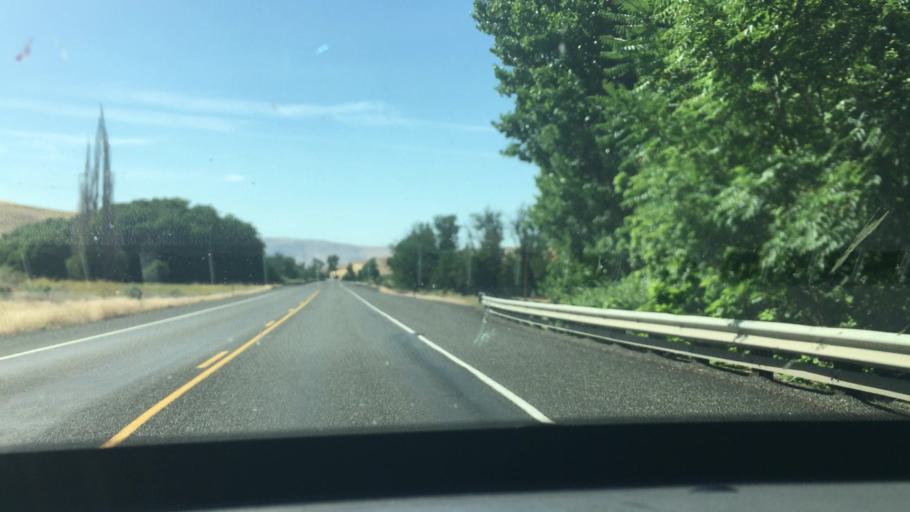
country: US
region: Oregon
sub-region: Sherman County
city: Moro
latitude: 45.6203
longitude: -120.7402
